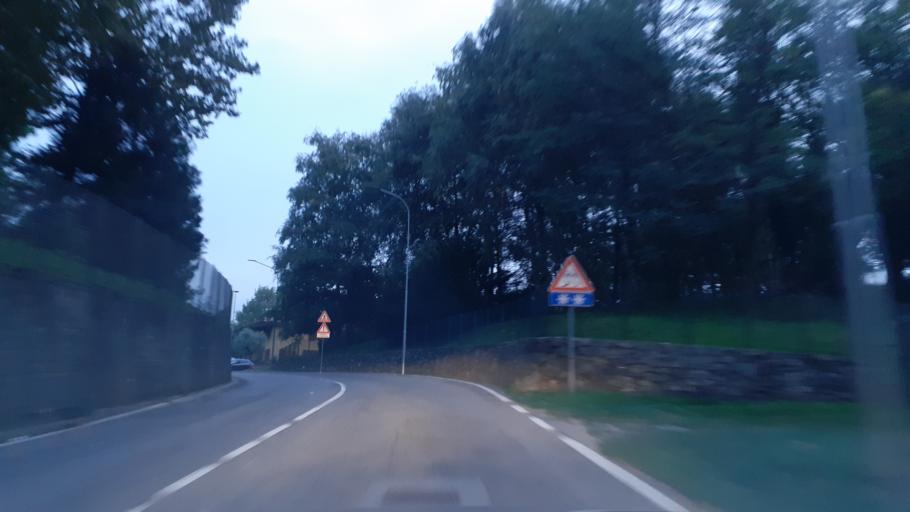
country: IT
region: Lombardy
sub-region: Provincia di Lecco
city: Garbagnate
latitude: 45.7607
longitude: 9.2922
